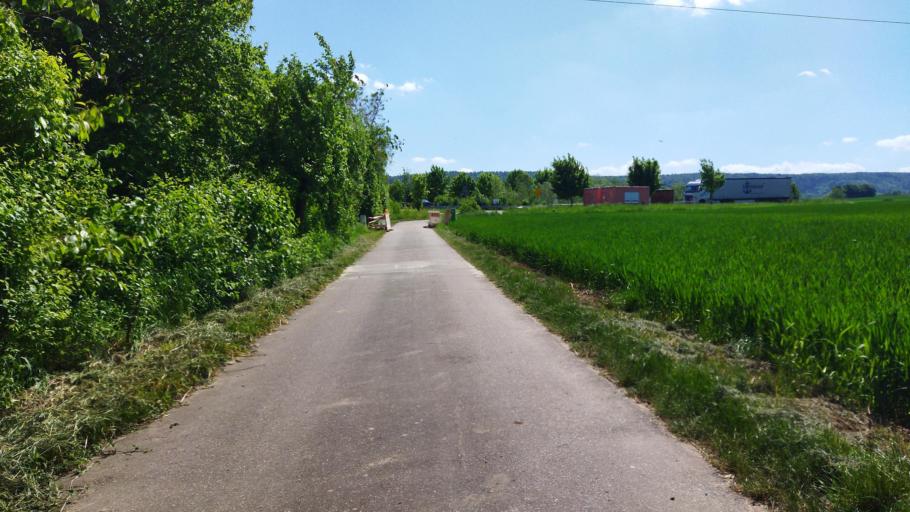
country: DE
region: Baden-Wuerttemberg
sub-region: Regierungsbezirk Stuttgart
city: Guglingen
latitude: 49.0614
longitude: 8.9926
